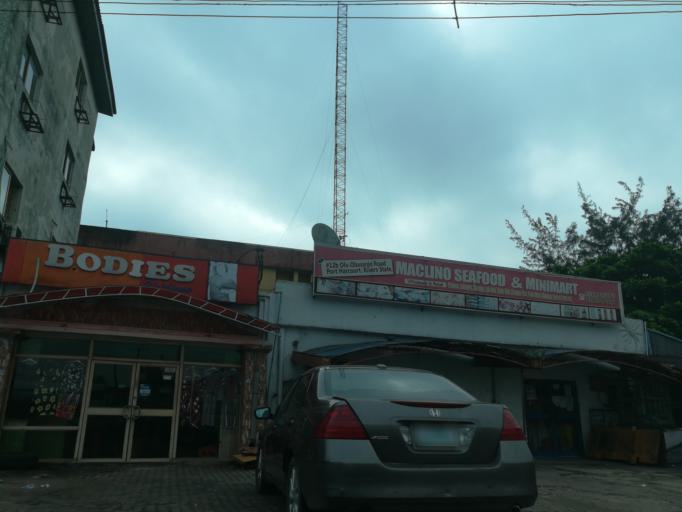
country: NG
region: Rivers
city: Port Harcourt
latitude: 4.8130
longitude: 7.0035
